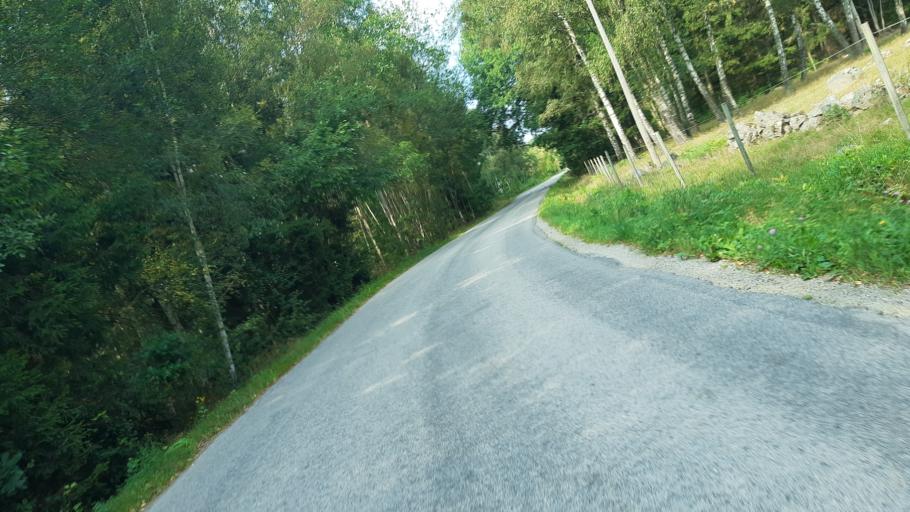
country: SE
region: Blekinge
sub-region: Karlskrona Kommun
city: Nattraby
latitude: 56.1769
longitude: 15.4733
